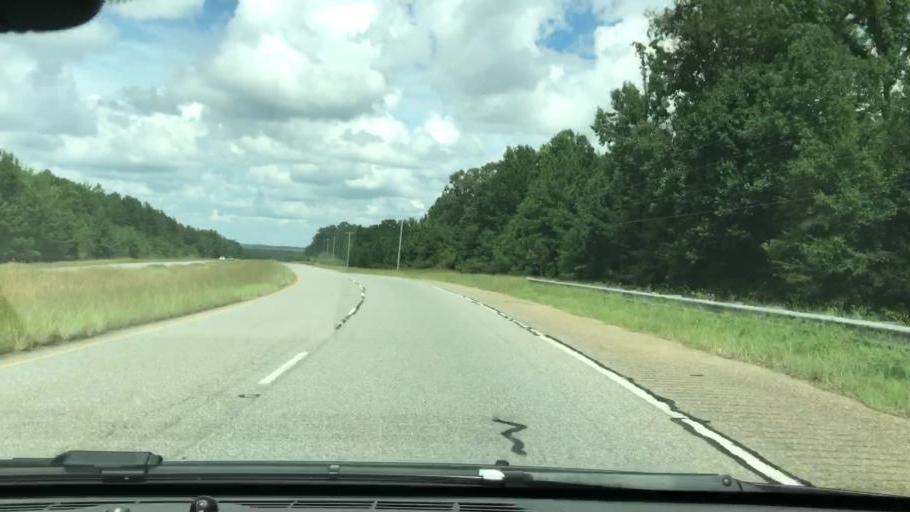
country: US
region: Georgia
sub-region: Stewart County
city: Lumpkin
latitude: 32.1181
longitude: -84.8148
